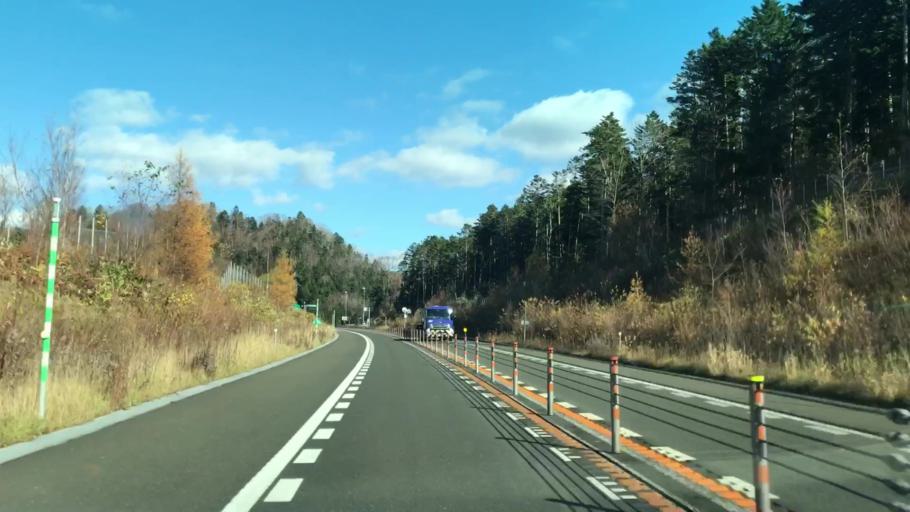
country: JP
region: Hokkaido
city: Shimo-furano
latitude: 42.9471
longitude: 142.2306
